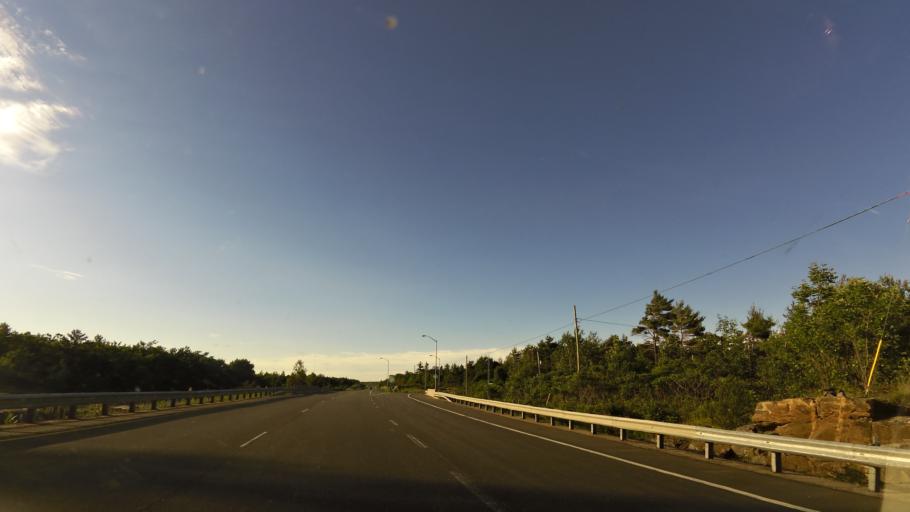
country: CA
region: Ontario
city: Midland
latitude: 44.9174
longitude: -79.7751
